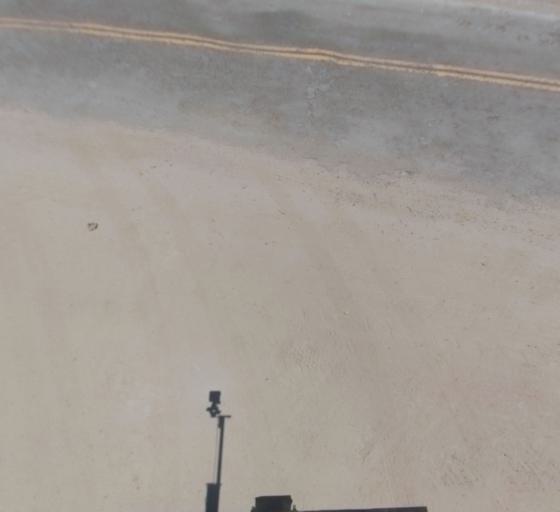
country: US
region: California
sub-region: Madera County
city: Parkwood
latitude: 36.8655
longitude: -120.1830
